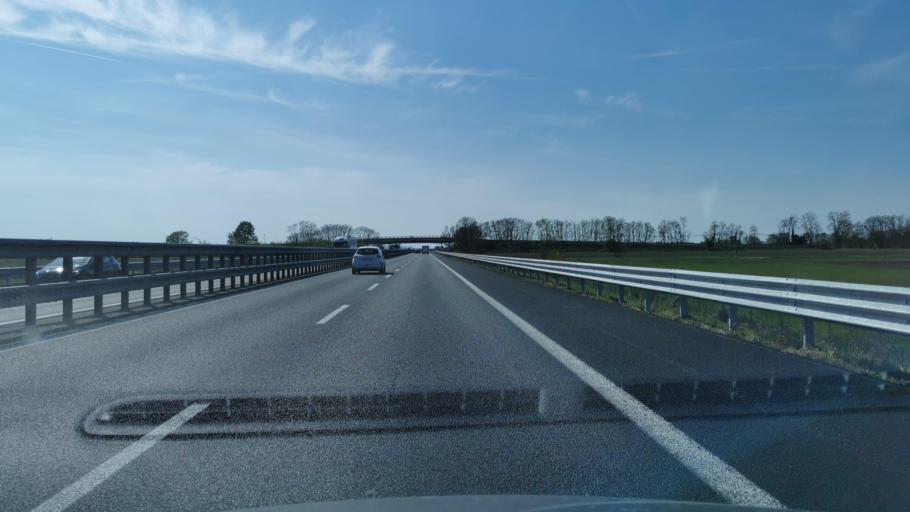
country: IT
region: Emilia-Romagna
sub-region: Provincia di Piacenza
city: Rottofreno
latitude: 45.0649
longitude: 9.5671
